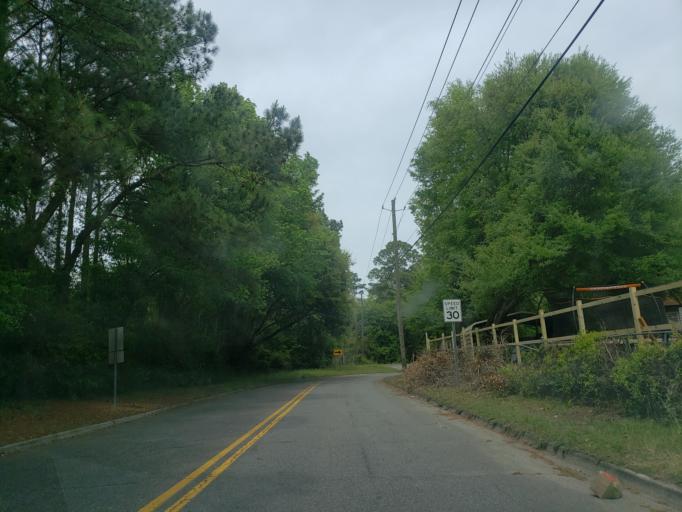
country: US
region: Georgia
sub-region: Chatham County
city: Georgetown
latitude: 31.9912
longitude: -81.1656
